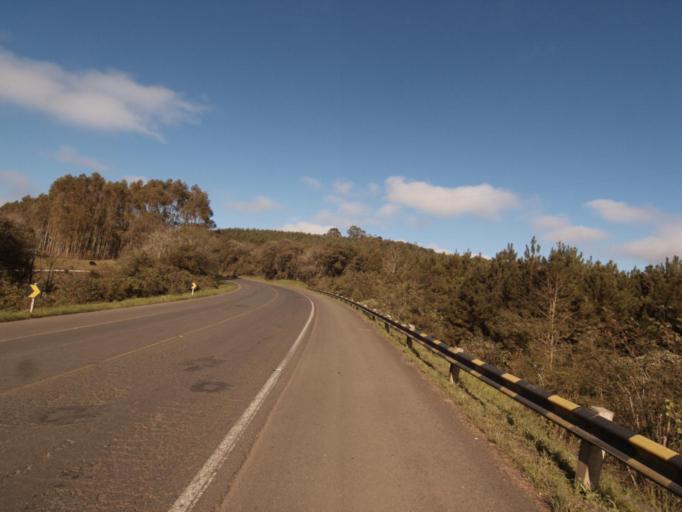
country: BR
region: Rio Grande do Sul
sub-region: Frederico Westphalen
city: Frederico Westphalen
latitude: -27.0482
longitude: -53.2293
